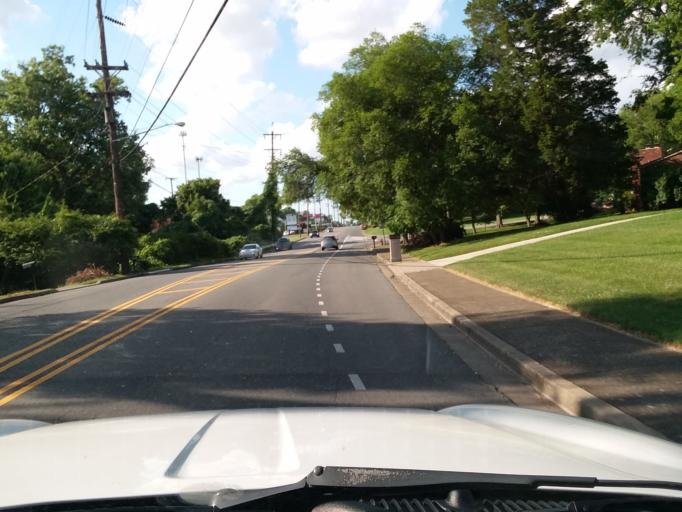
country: US
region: Tennessee
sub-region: Davidson County
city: Oak Hill
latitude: 36.0740
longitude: -86.7592
